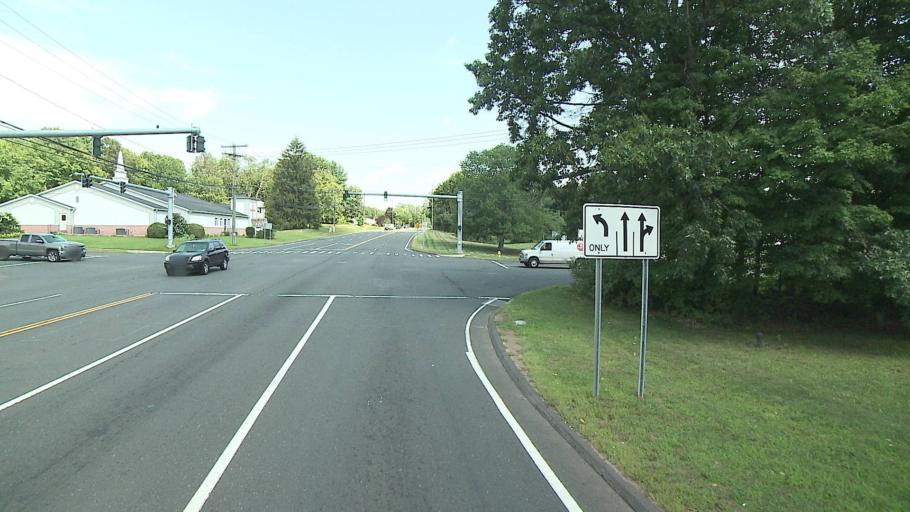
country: US
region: Connecticut
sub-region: Hartford County
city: Plainville
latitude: 41.6917
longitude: -72.8771
